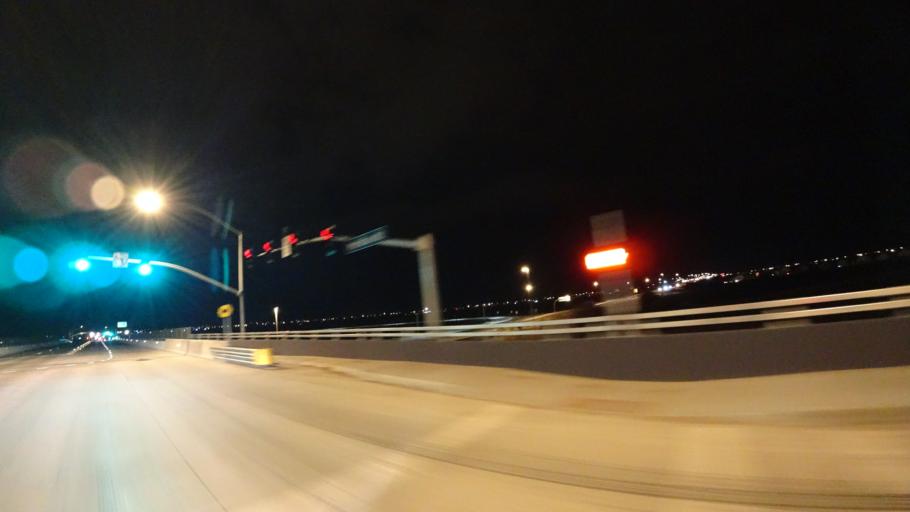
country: US
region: Arizona
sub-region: Pinal County
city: Apache Junction
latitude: 33.3859
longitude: -111.5807
